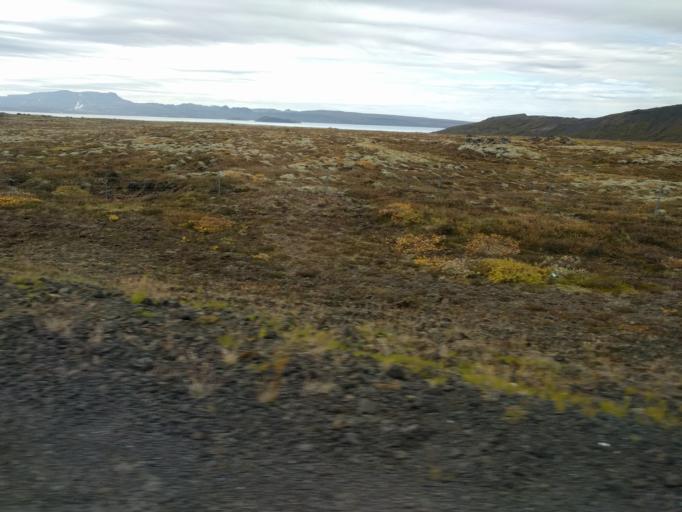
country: IS
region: South
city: Hveragerdi
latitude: 64.2132
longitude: -21.0476
